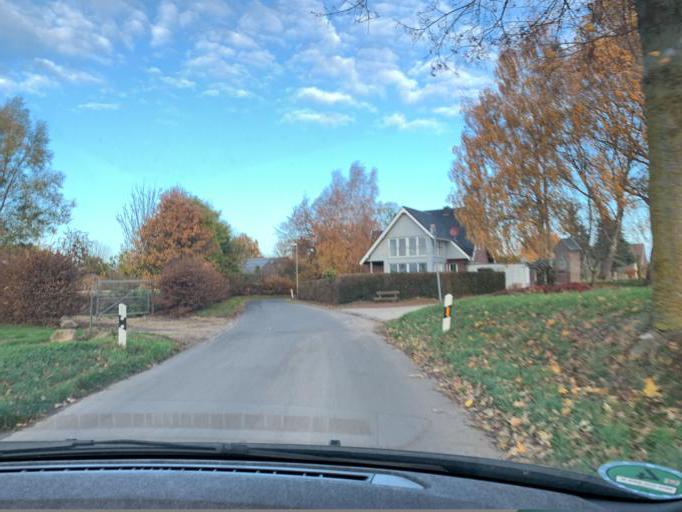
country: DE
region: North Rhine-Westphalia
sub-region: Regierungsbezirk Koln
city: Titz
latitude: 51.0418
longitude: 6.4077
